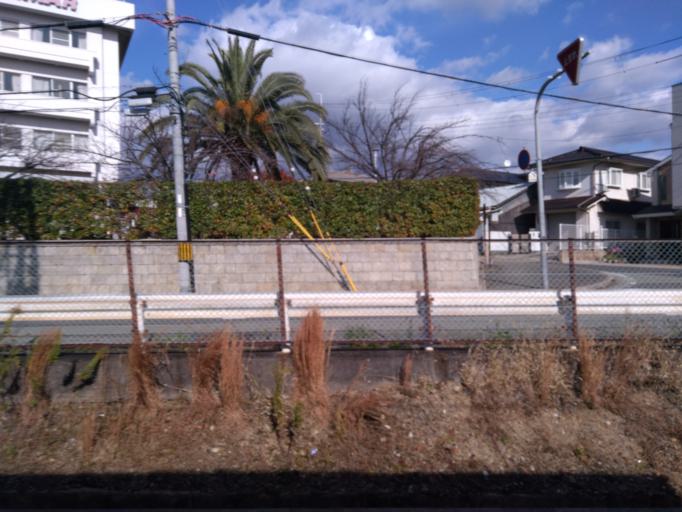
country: JP
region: Hyogo
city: Kawanishi
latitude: 34.8278
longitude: 135.4068
